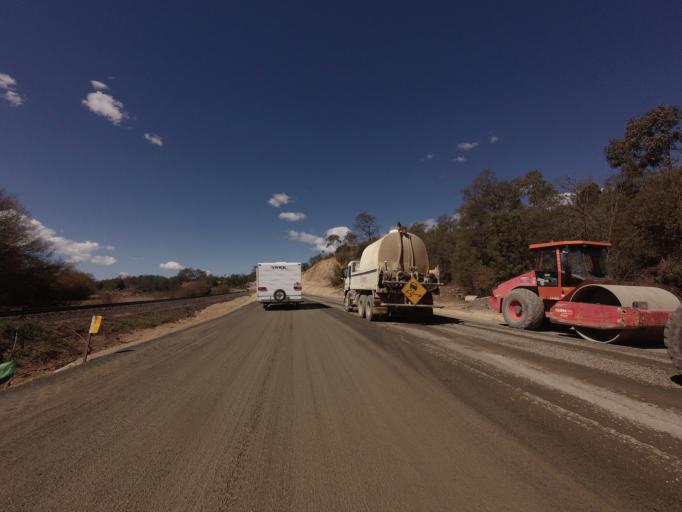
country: AU
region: Tasmania
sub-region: Break O'Day
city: St Helens
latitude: -41.6505
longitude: 147.9306
